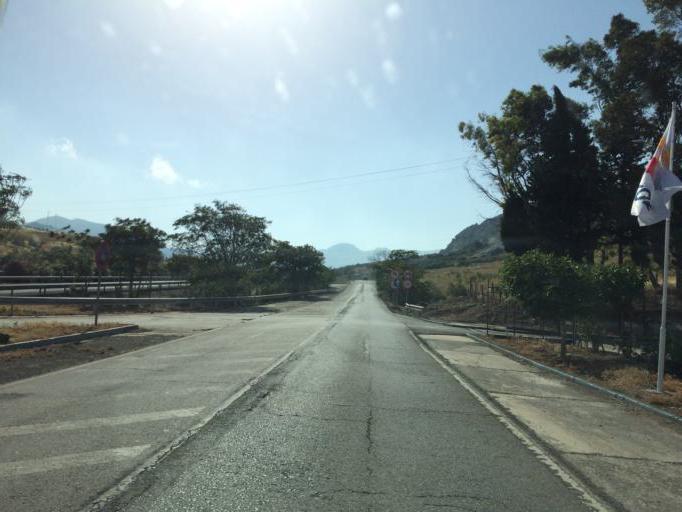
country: ES
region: Andalusia
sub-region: Provincia de Malaga
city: Villanueva del Rosario
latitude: 36.9809
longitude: -4.4559
